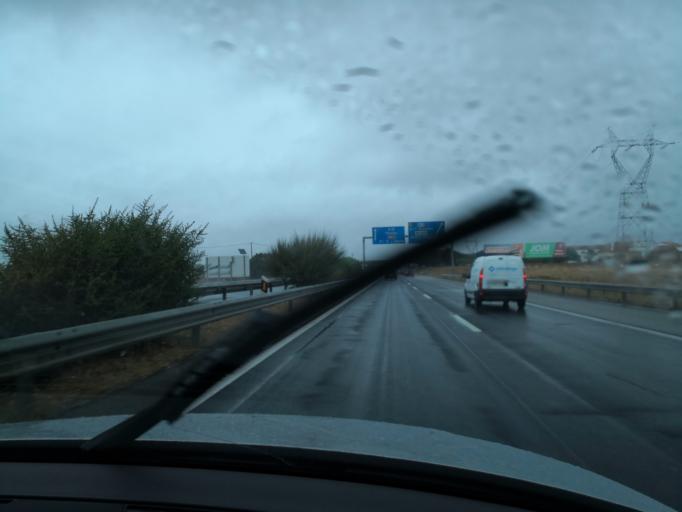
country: PT
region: Setubal
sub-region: Montijo
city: Montijo
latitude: 38.6709
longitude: -8.9513
